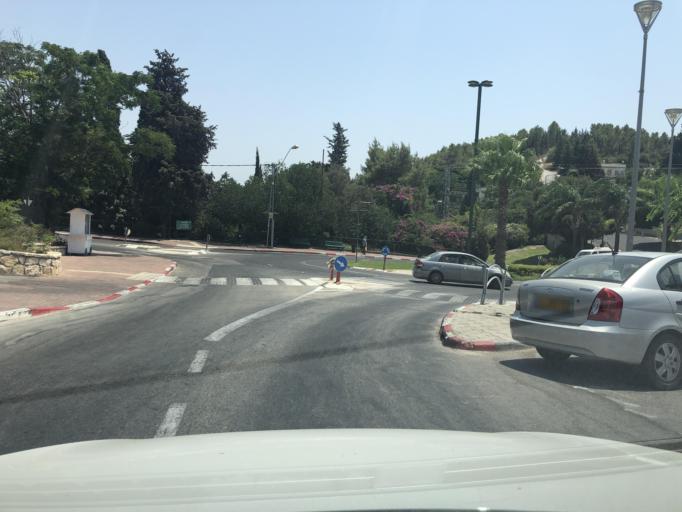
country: IL
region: Haifa
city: Daliyat el Karmil
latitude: 32.6594
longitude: 35.1087
